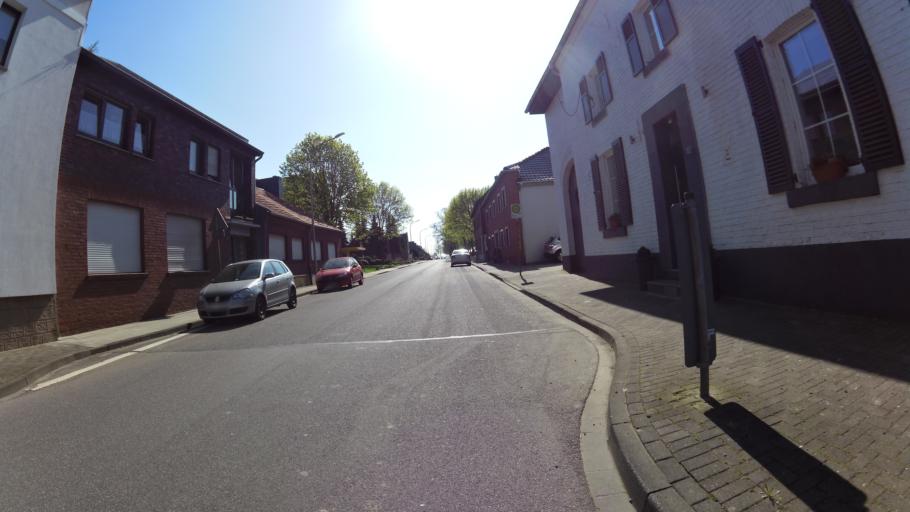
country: DE
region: North Rhine-Westphalia
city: Baesweiler
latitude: 50.9513
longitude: 6.1723
